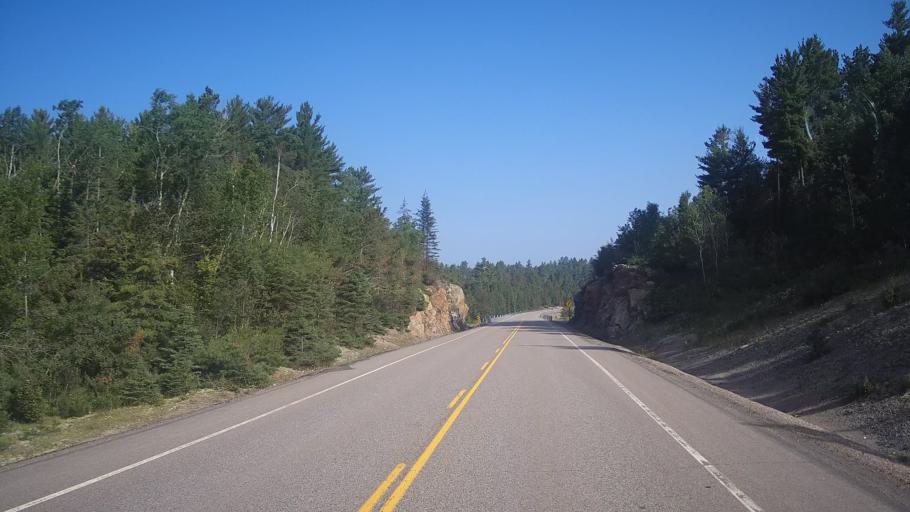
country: CA
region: Ontario
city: Rayside-Balfour
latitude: 46.7426
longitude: -81.5983
